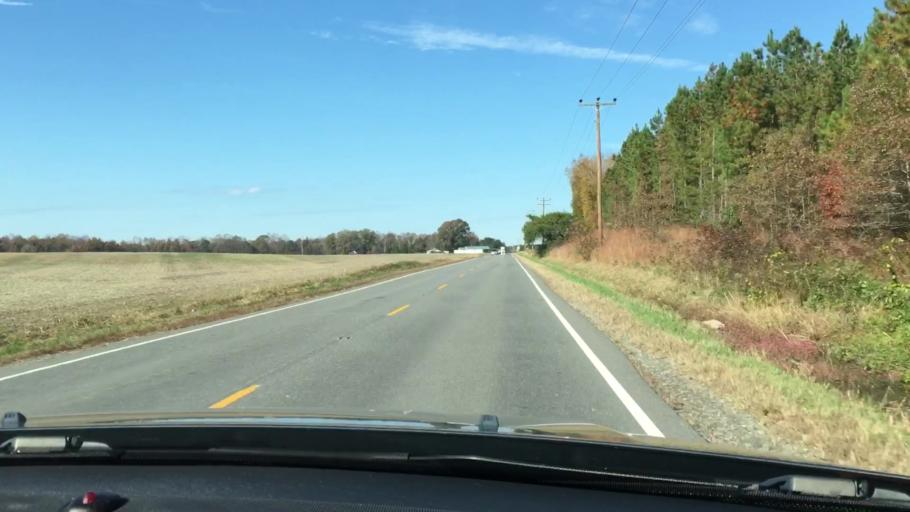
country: US
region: Virginia
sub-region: King and Queen County
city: King and Queen Court House
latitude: 37.6277
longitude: -76.9318
